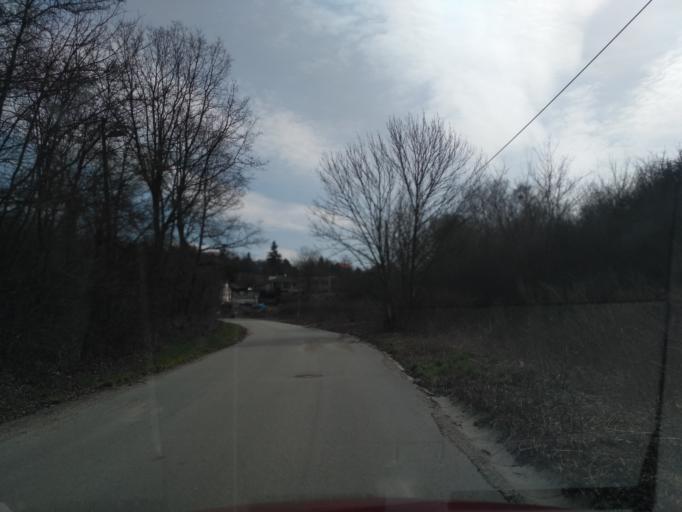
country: SK
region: Kosicky
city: Kosice
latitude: 48.7244
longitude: 21.2865
